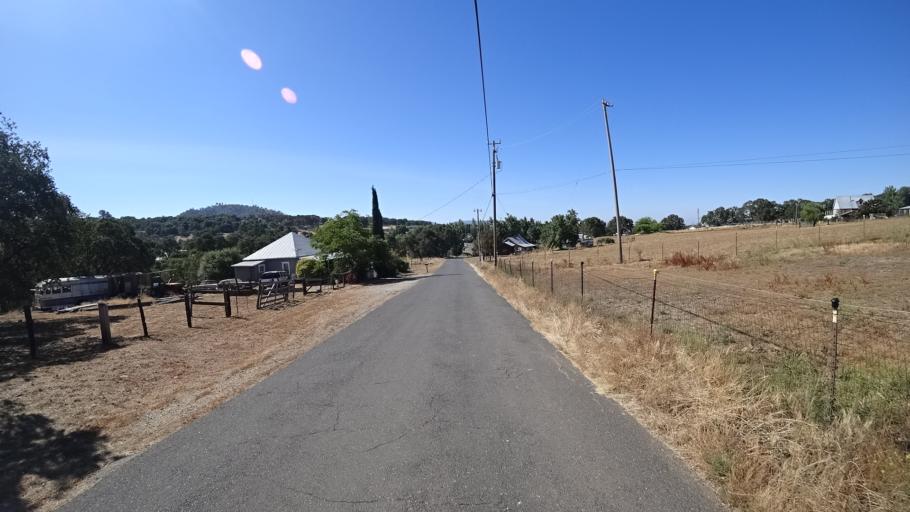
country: US
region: California
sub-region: Amador County
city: Jackson
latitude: 38.2618
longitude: -120.7638
